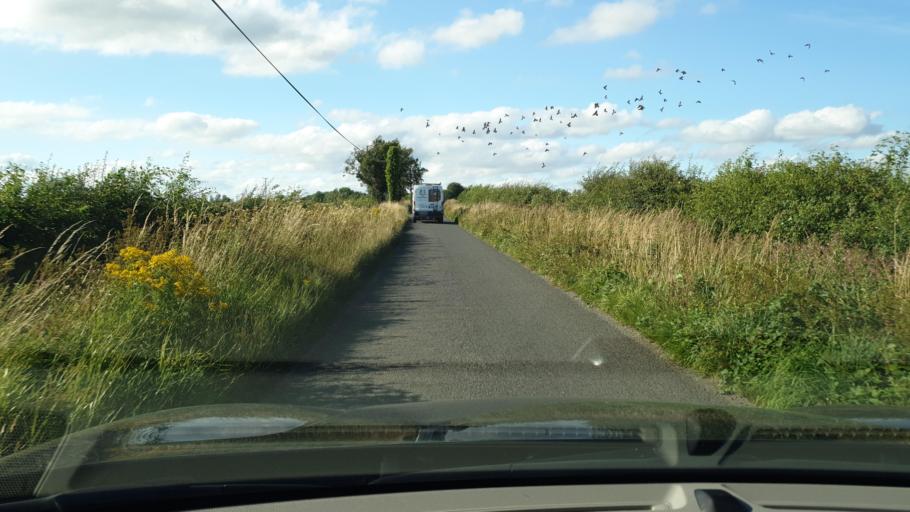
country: IE
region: Leinster
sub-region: An Mhi
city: Ashbourne
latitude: 53.5197
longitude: -6.3857
